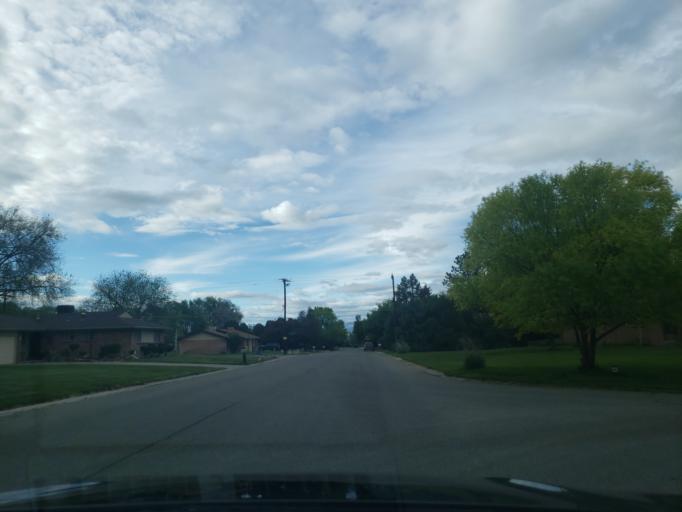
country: US
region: Colorado
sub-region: Mesa County
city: Redlands
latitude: 39.0967
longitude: -108.6586
